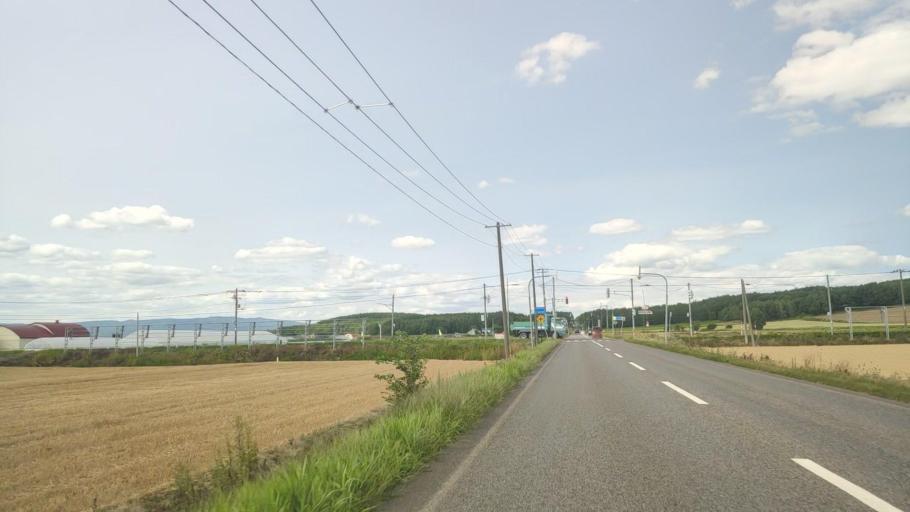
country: JP
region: Hokkaido
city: Nayoro
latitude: 44.2352
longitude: 142.4157
